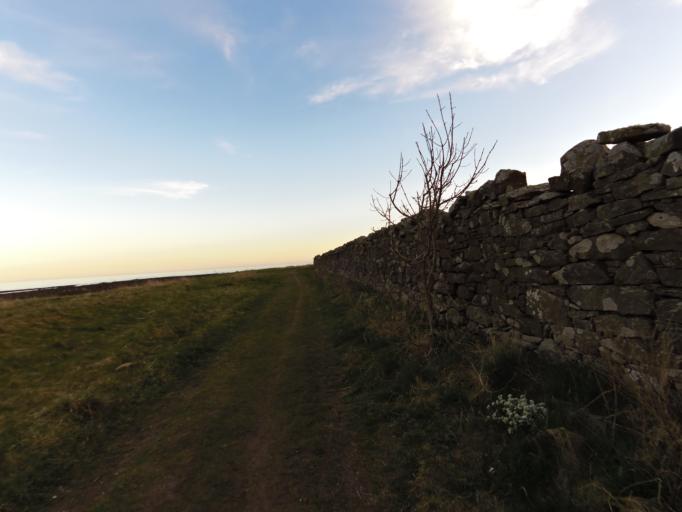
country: GB
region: Scotland
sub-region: Aberdeenshire
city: Inverbervie
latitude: 56.8035
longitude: -2.3150
